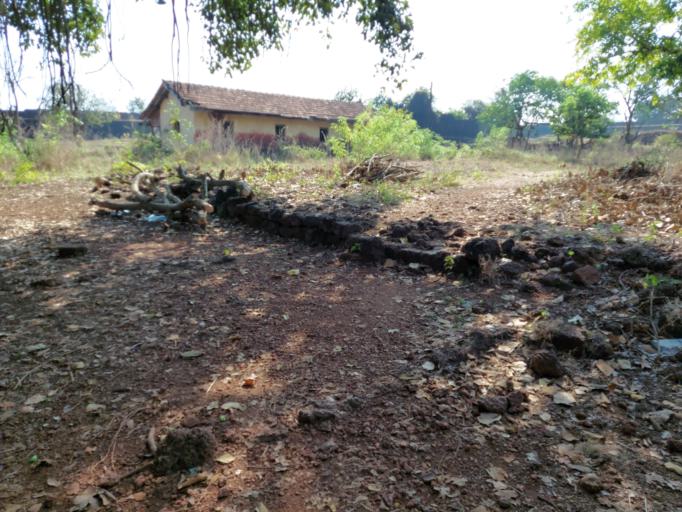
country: IN
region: Maharashtra
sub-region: Ratnagiri
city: Guhagar
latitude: 17.3016
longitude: 73.2210
